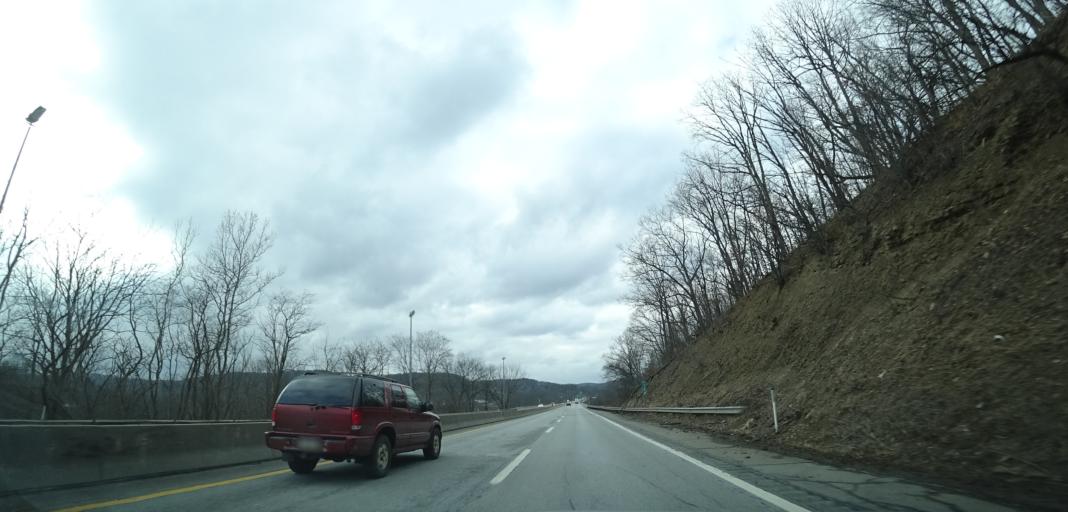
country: US
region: Pennsylvania
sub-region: Beaver County
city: West Mayfield
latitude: 40.8100
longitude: -80.3147
